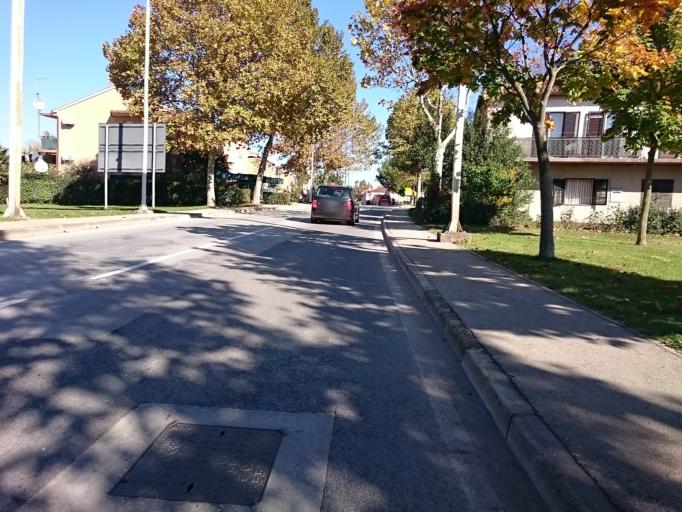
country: HR
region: Istarska
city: Umag
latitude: 45.4373
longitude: 13.5288
